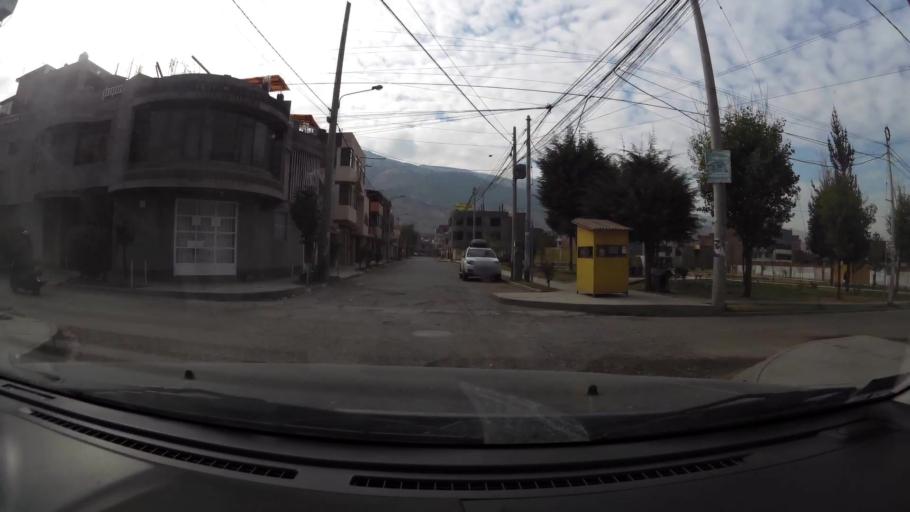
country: PE
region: Junin
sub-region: Provincia de Huancayo
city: Huancayo
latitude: -12.0482
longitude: -75.1948
